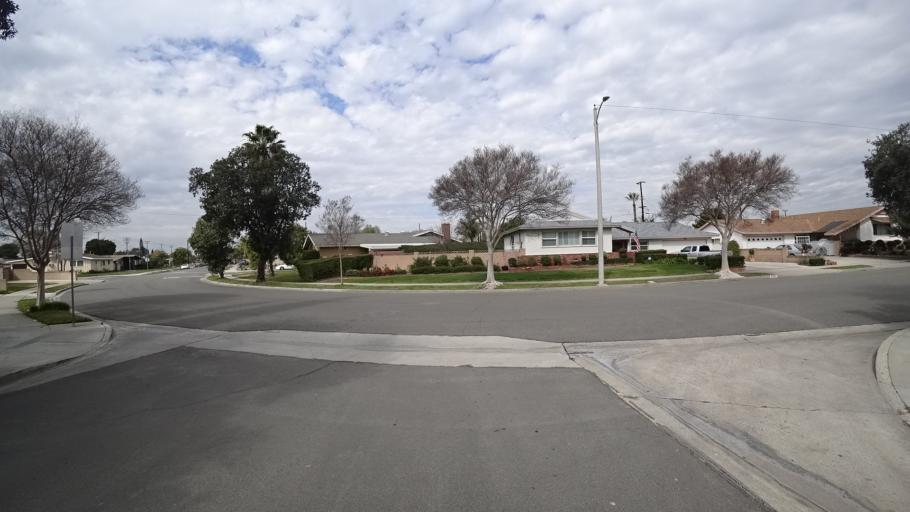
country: US
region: California
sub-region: Orange County
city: Anaheim
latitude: 33.8423
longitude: -117.8841
